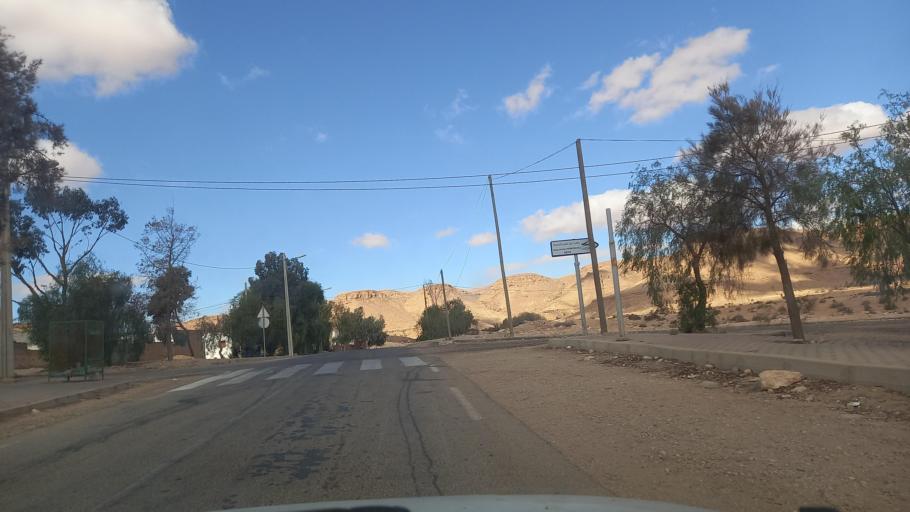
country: TN
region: Tataouine
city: Tataouine
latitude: 32.9148
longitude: 10.2788
